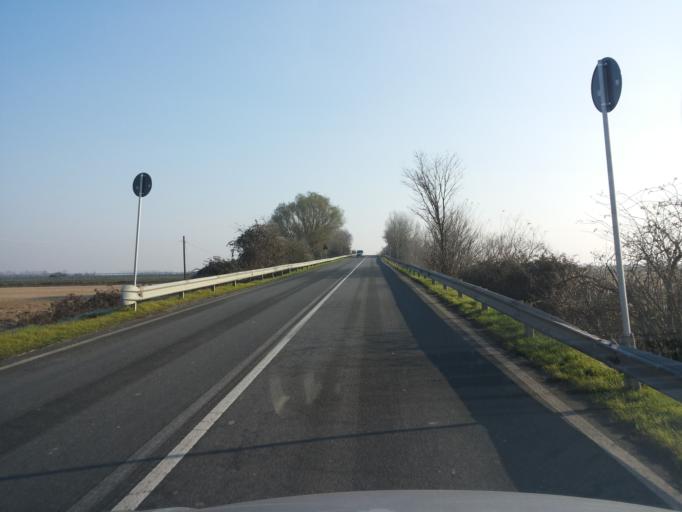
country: IT
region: Piedmont
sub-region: Provincia di Vercelli
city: Stroppiana
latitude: 45.2265
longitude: 8.4732
